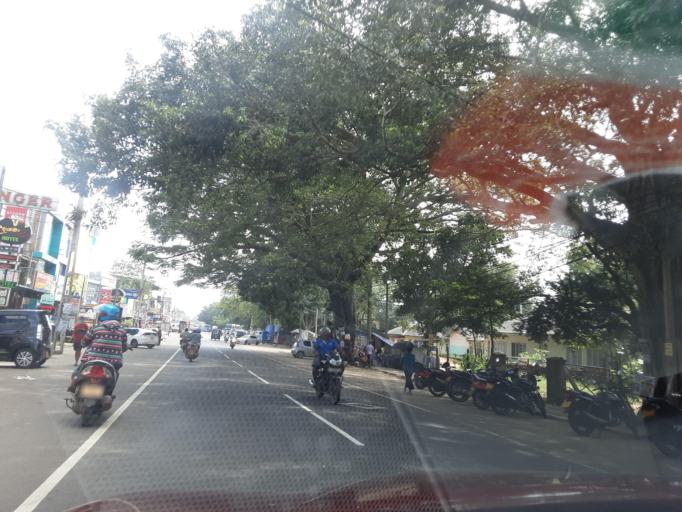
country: LK
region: Northern Province
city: Vavuniya
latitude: 8.5408
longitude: 80.4921
